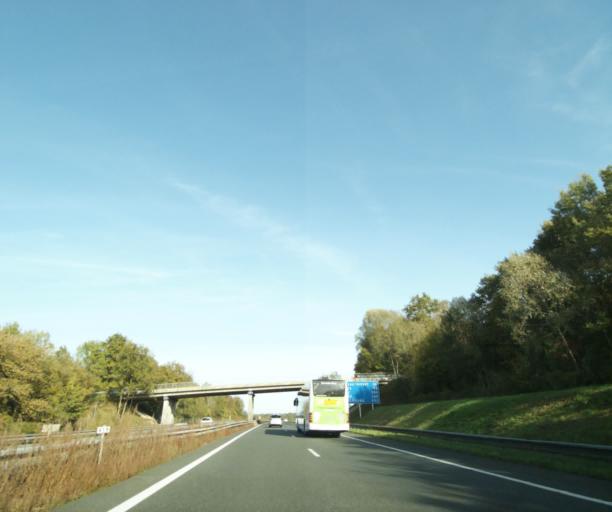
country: FR
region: Ile-de-France
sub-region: Departement de Seine-et-Marne
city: Bouleurs
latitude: 48.8934
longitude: 2.9073
